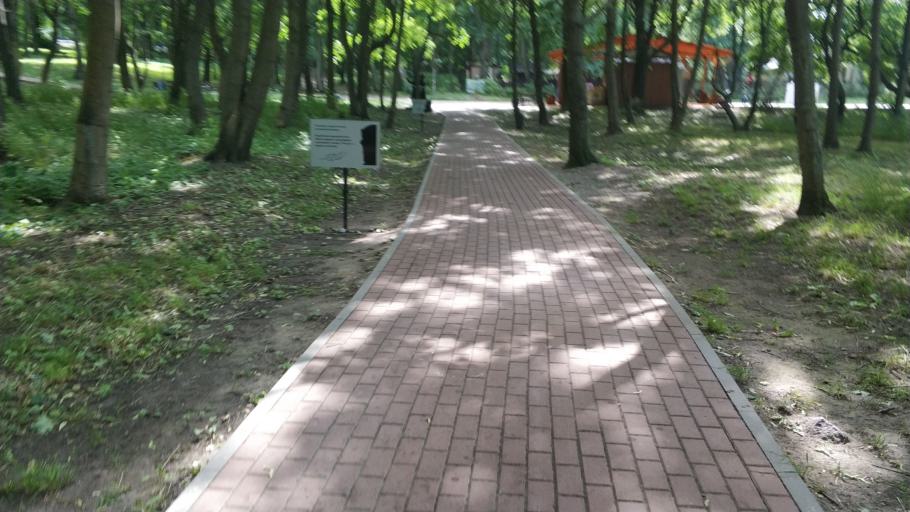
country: RU
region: Kaliningrad
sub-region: Gorod Kaliningrad
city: Yantarnyy
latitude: 54.8676
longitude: 19.9345
